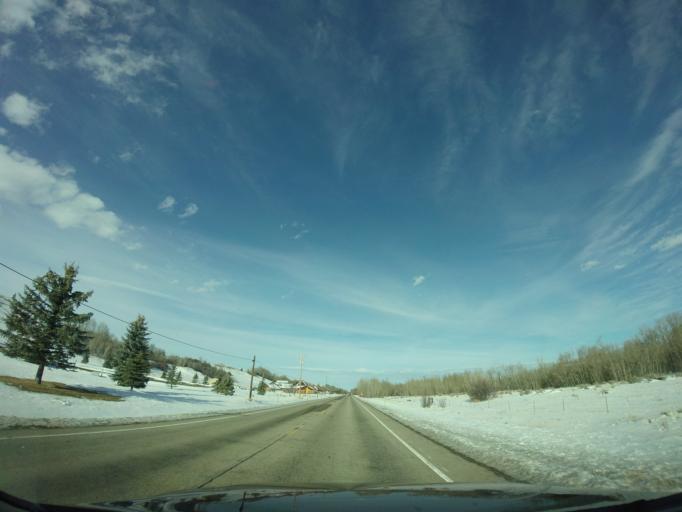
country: US
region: Montana
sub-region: Carbon County
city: Red Lodge
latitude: 45.2089
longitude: -109.2437
